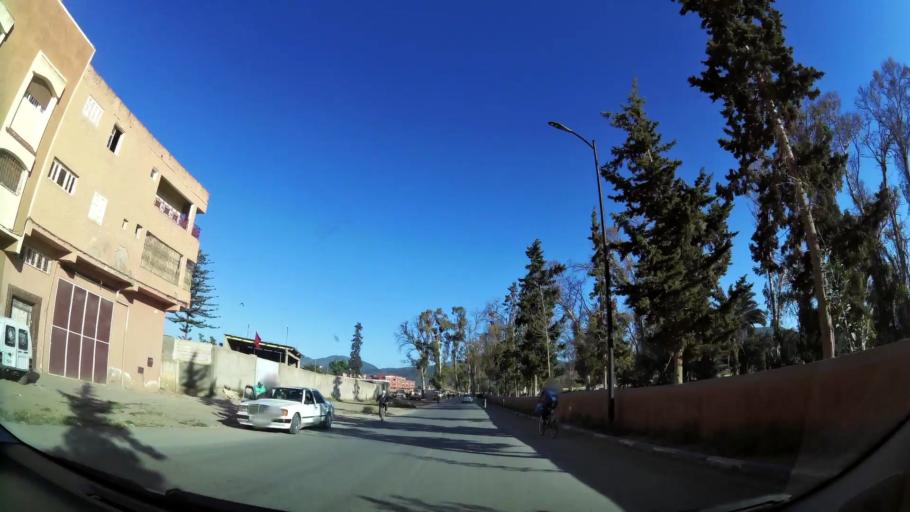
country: MA
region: Oriental
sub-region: Berkane-Taourirt
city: Berkane
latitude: 34.9236
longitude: -2.3398
